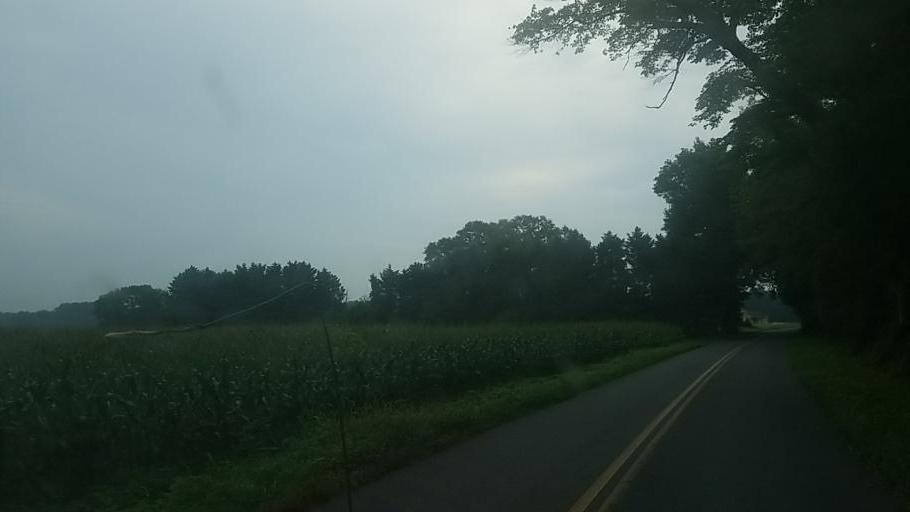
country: US
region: Delaware
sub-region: Sussex County
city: Selbyville
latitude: 38.4262
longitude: -75.2940
